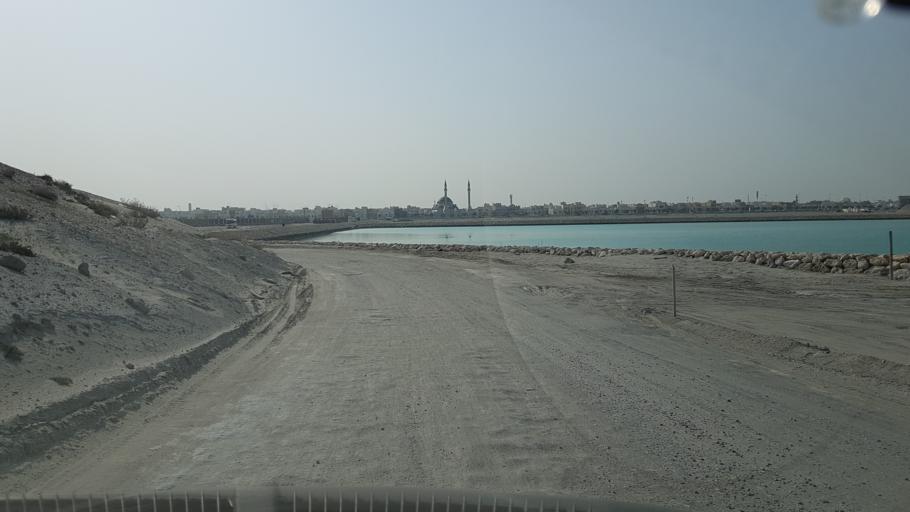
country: BH
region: Muharraq
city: Al Hadd
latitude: 26.2720
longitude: 50.6681
